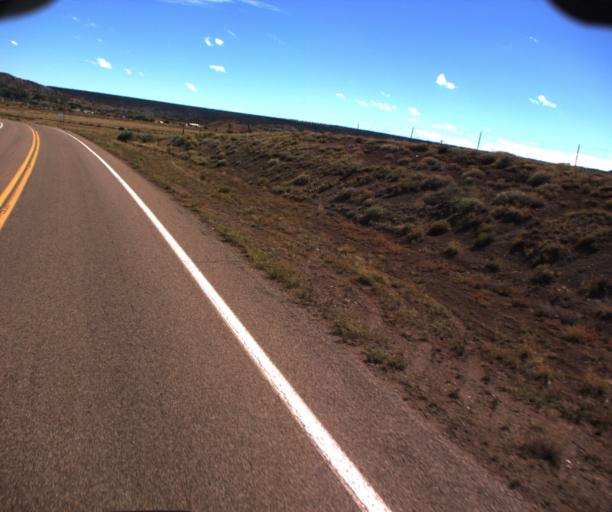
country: US
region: Arizona
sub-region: Apache County
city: Saint Johns
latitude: 34.4815
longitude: -109.6178
